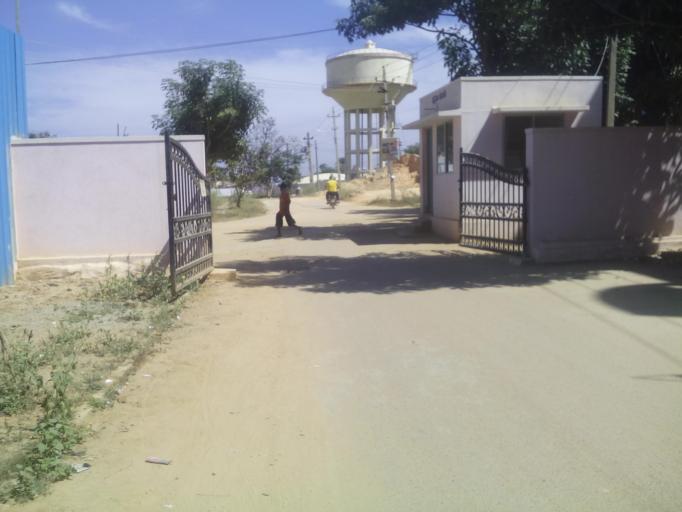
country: IN
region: Karnataka
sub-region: Bangalore Urban
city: Anekal
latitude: 12.7896
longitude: 77.7033
